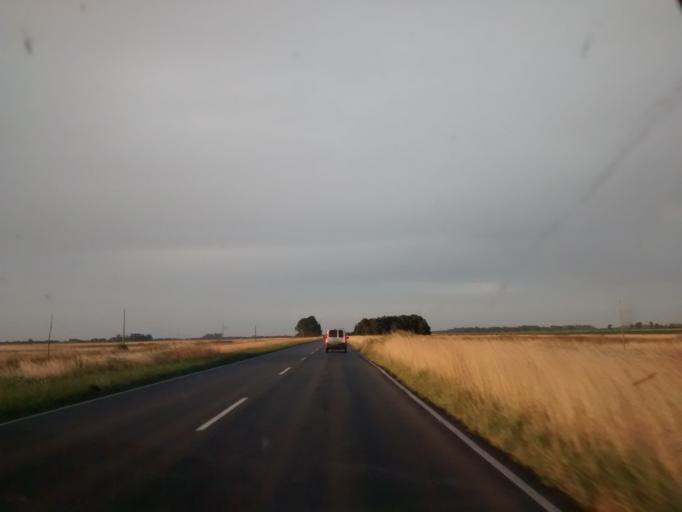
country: AR
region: Buenos Aires
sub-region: Partido de General Belgrano
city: General Belgrano
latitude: -35.9215
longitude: -58.6195
